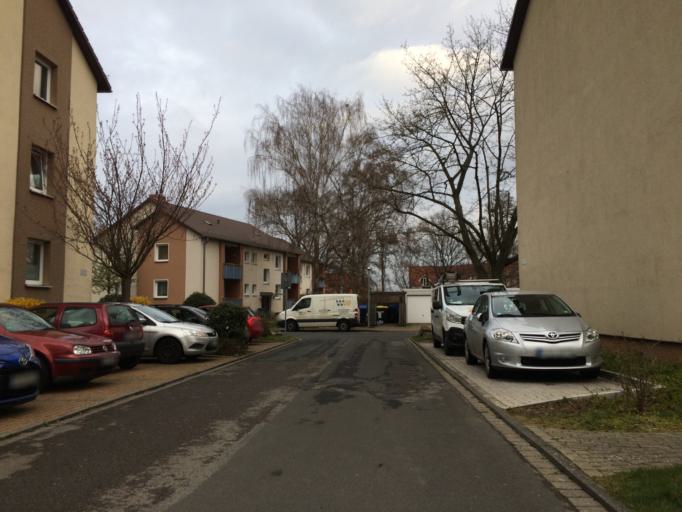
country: DE
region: Lower Saxony
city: Gehrden
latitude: 52.3057
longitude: 9.6065
